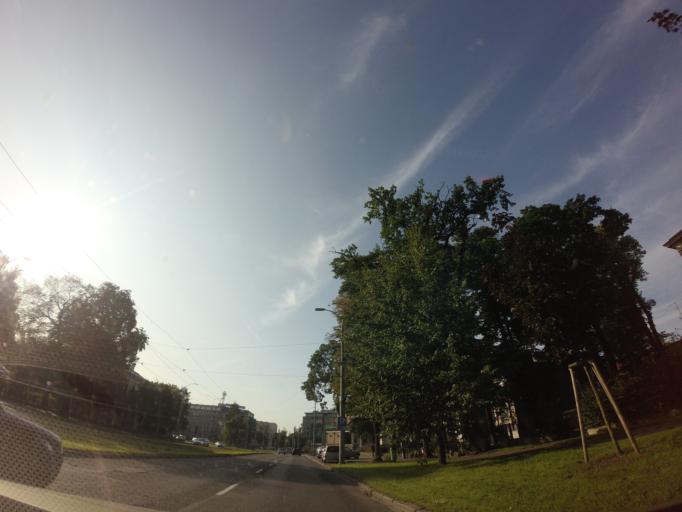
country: PL
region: West Pomeranian Voivodeship
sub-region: Szczecin
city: Szczecin
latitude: 53.4340
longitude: 14.5393
